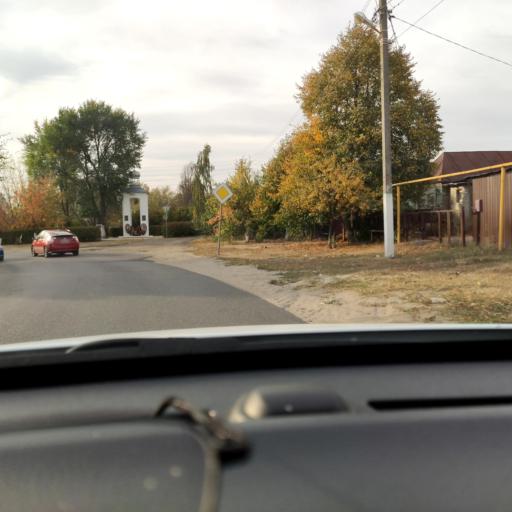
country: RU
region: Voronezj
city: Somovo
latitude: 51.6895
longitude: 39.3187
